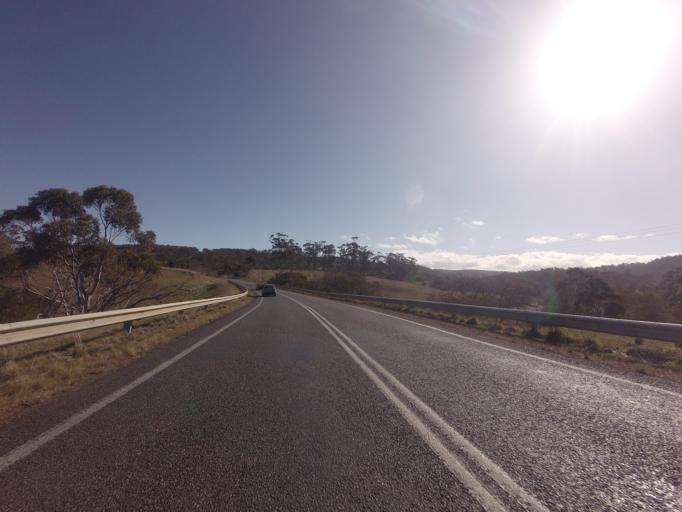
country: AU
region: Tasmania
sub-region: Sorell
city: Sorell
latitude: -42.2127
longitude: 148.0344
